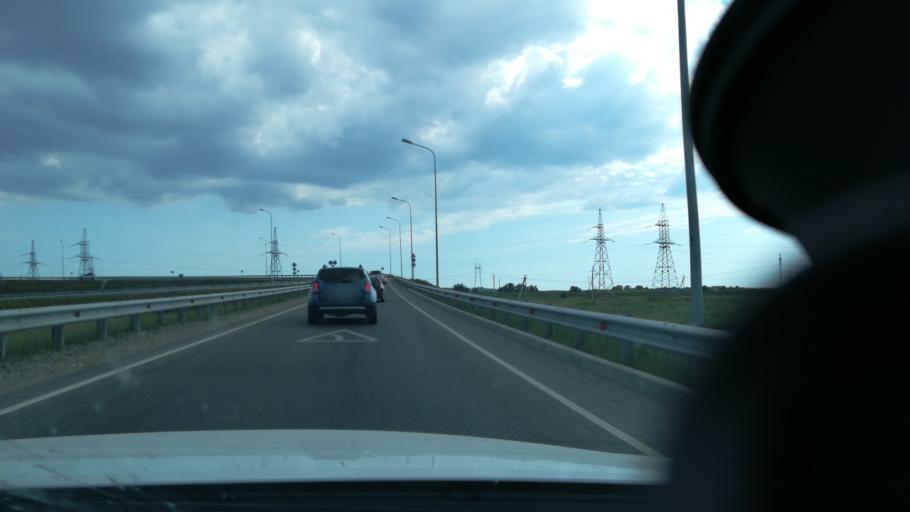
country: RU
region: Krasnodarskiy
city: Dzhiginka
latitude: 45.1390
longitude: 37.3160
